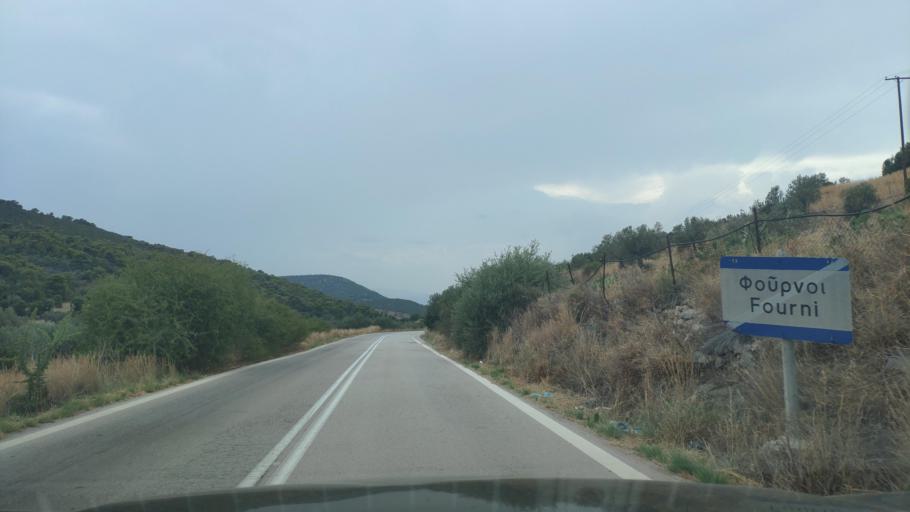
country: GR
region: Peloponnese
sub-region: Nomos Argolidos
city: Didyma
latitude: 37.4315
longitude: 23.1664
